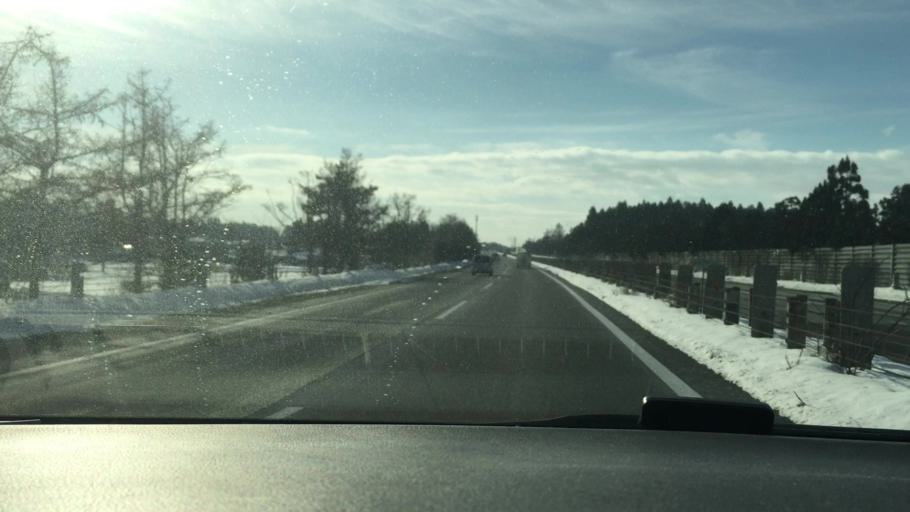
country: JP
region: Iwate
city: Hanamaki
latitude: 39.3506
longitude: 141.0896
